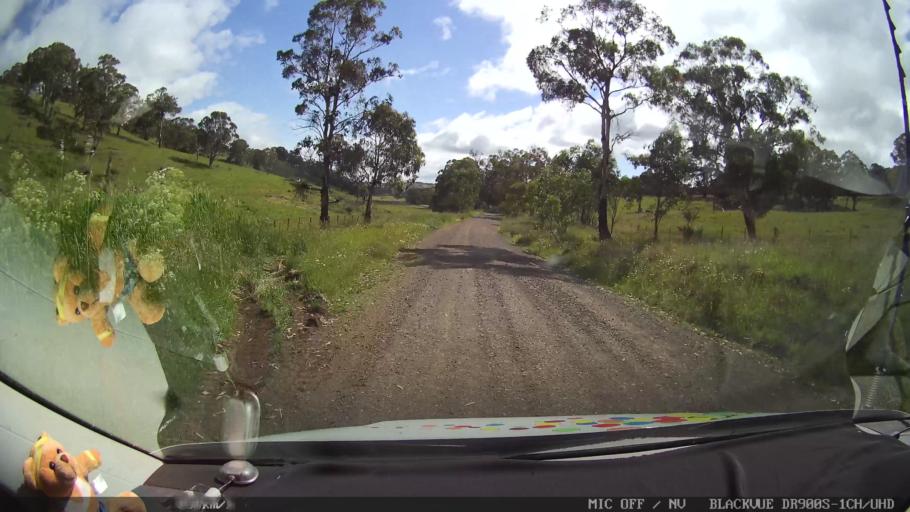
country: AU
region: New South Wales
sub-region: Guyra
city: Guyra
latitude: -29.9985
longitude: 151.6759
